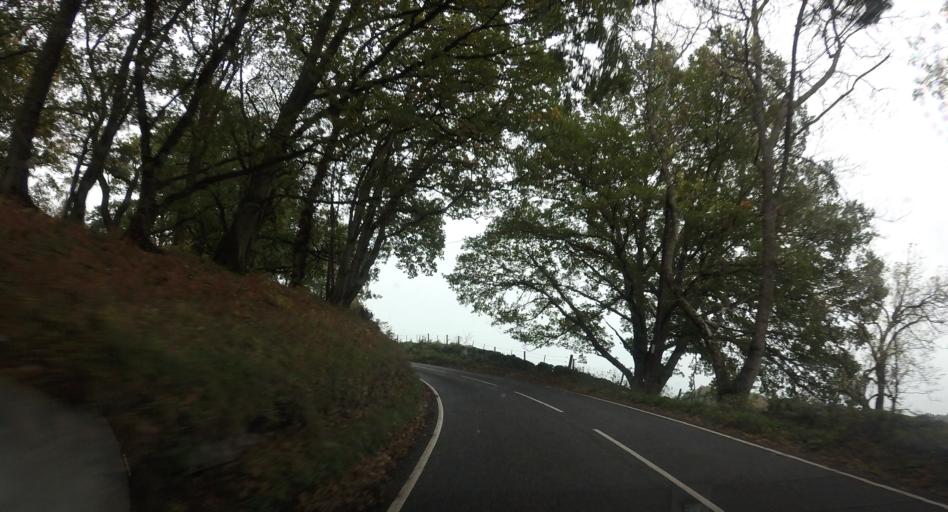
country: GB
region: Scotland
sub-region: Perth and Kinross
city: Bankfoot
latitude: 56.5504
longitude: -3.5528
